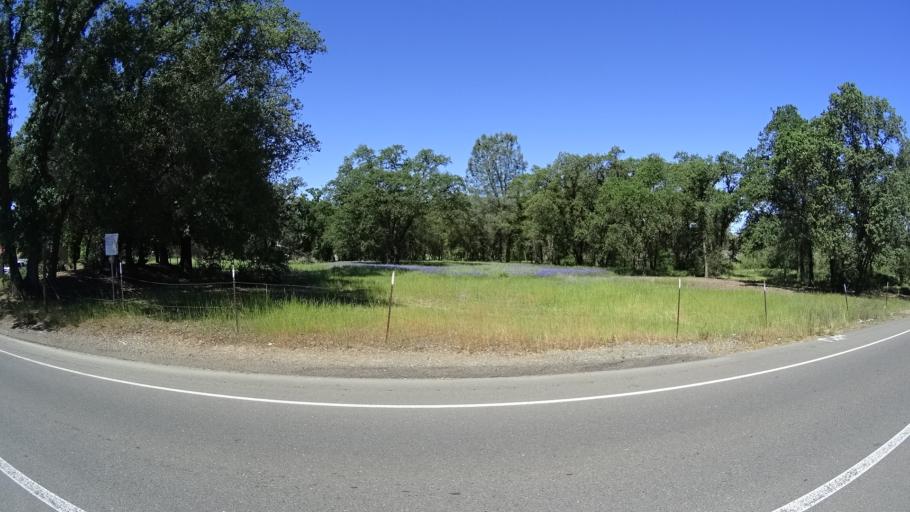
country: US
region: California
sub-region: Placer County
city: Loomis
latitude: 38.8070
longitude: -121.2056
